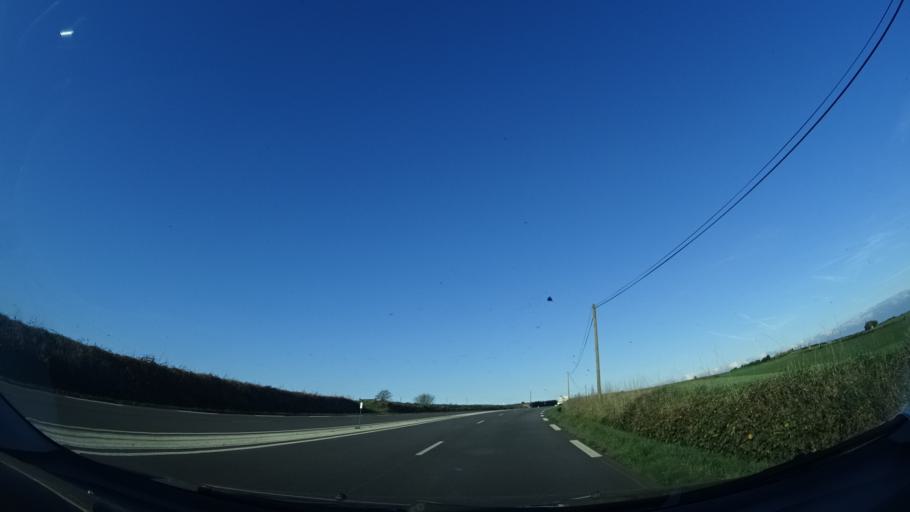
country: FR
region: Brittany
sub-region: Departement du Finistere
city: Saint-Pol-de-Leon
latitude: 48.6516
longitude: -3.9619
